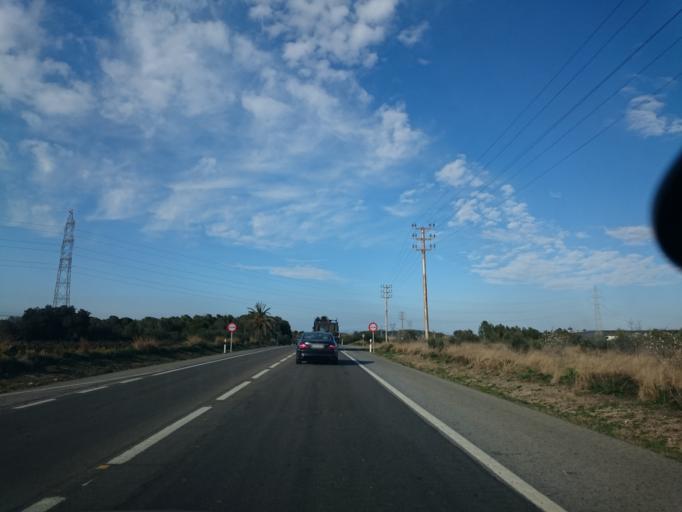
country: ES
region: Catalonia
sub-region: Provincia de Barcelona
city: Castellet
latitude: 41.2802
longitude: 1.6132
